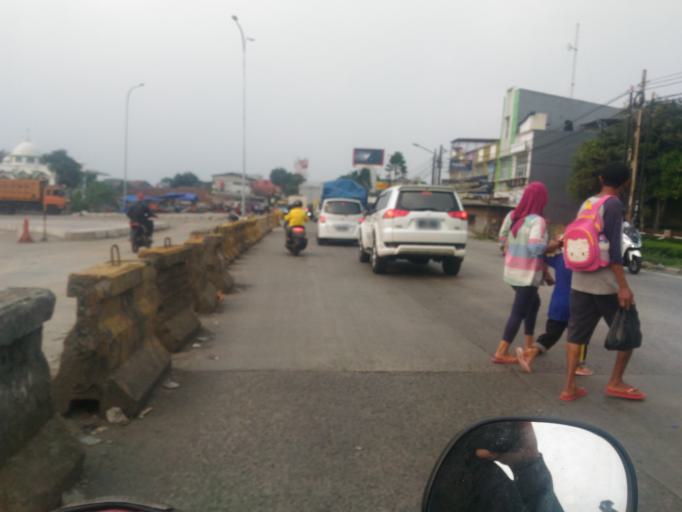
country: ID
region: West Java
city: Caringin
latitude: -6.6597
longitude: 106.8453
